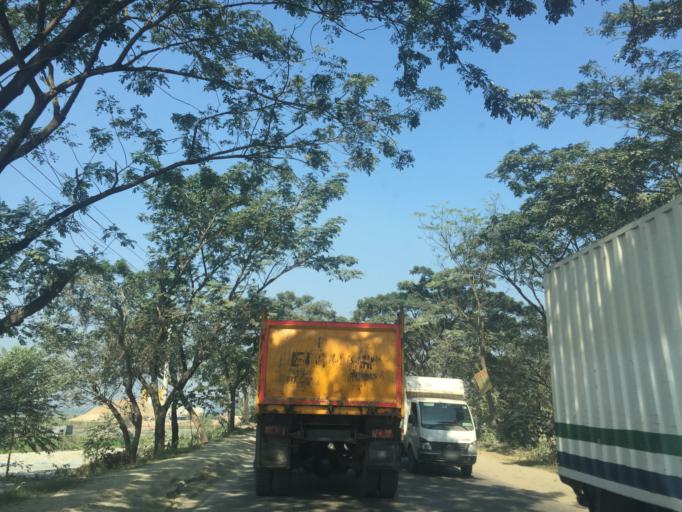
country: BD
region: Dhaka
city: Tungi
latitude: 23.8321
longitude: 90.3405
